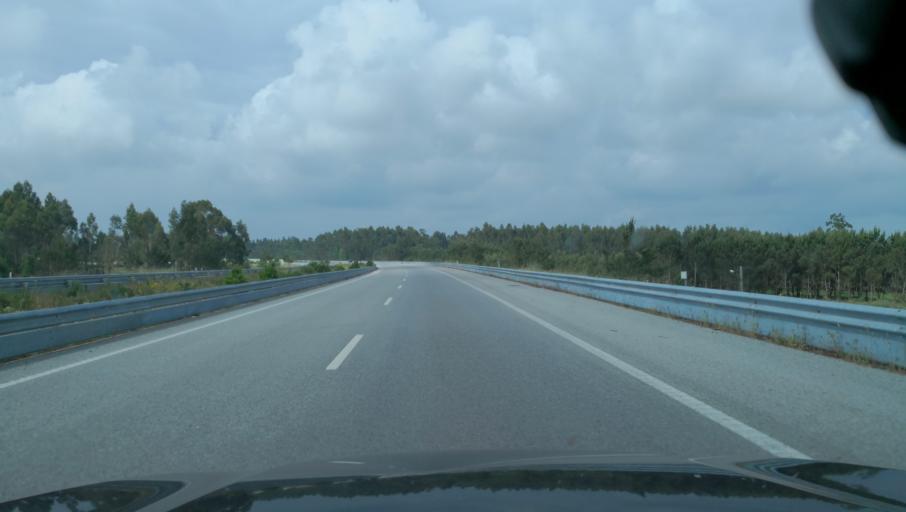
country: PT
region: Coimbra
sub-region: Montemor-O-Velho
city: Arazede
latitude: 40.3037
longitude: -8.7357
